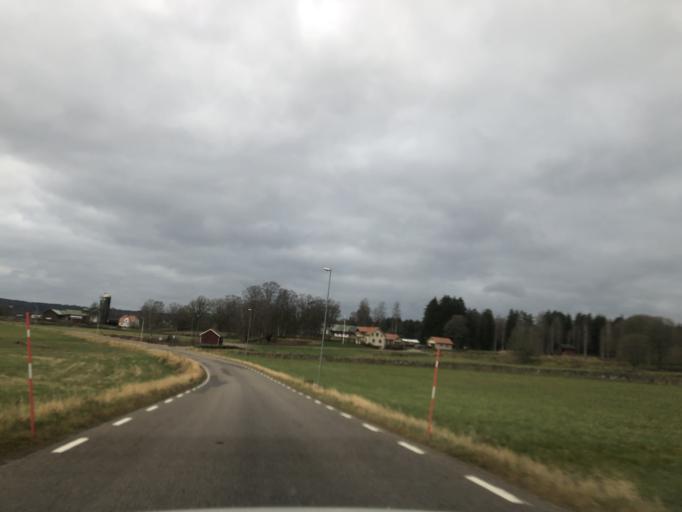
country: SE
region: Vaestra Goetaland
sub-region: Boras Kommun
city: Dalsjofors
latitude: 57.8290
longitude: 13.1751
